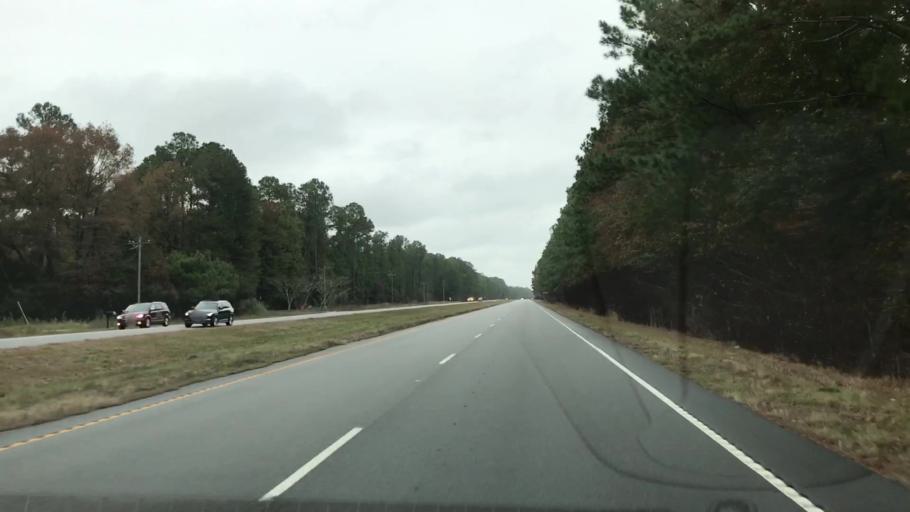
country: US
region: South Carolina
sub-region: Charleston County
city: Awendaw
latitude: 33.1262
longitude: -79.4490
